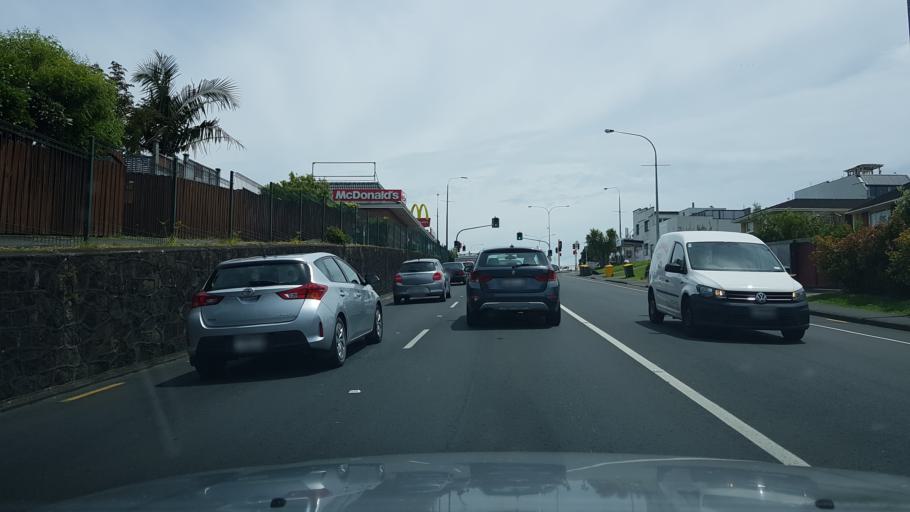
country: NZ
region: Auckland
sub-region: Auckland
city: North Shore
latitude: -36.8092
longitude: 174.7906
